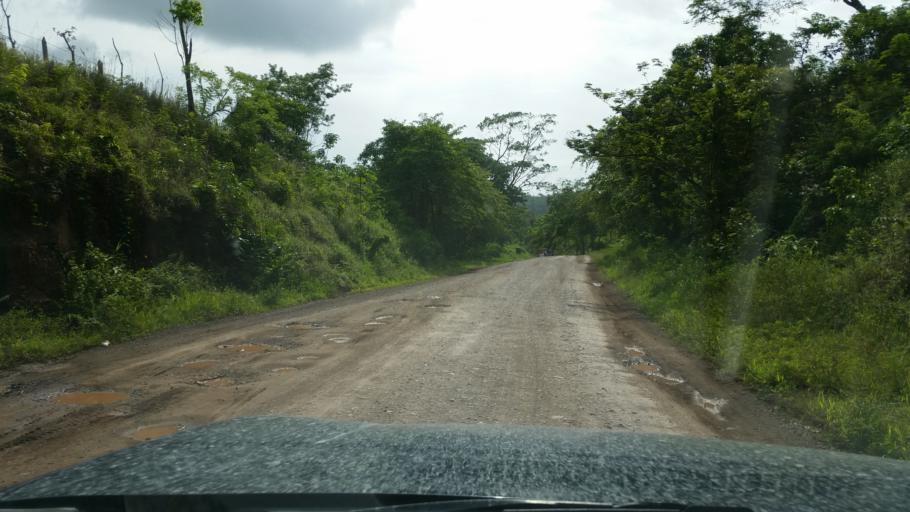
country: NI
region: Atlantico Norte (RAAN)
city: Siuna
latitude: 13.5937
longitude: -84.8086
